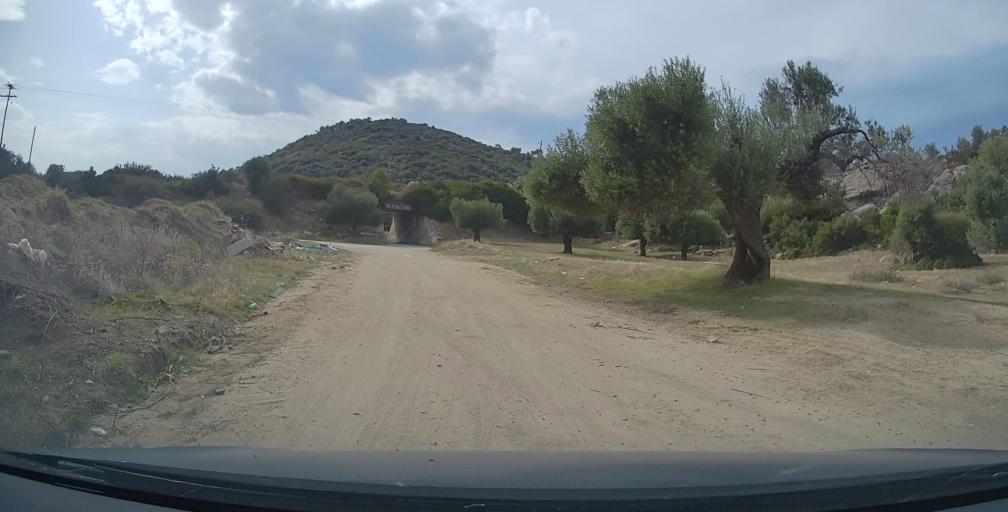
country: GR
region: Central Macedonia
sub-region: Nomos Chalkidikis
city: Sykia
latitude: 39.9891
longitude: 23.9124
